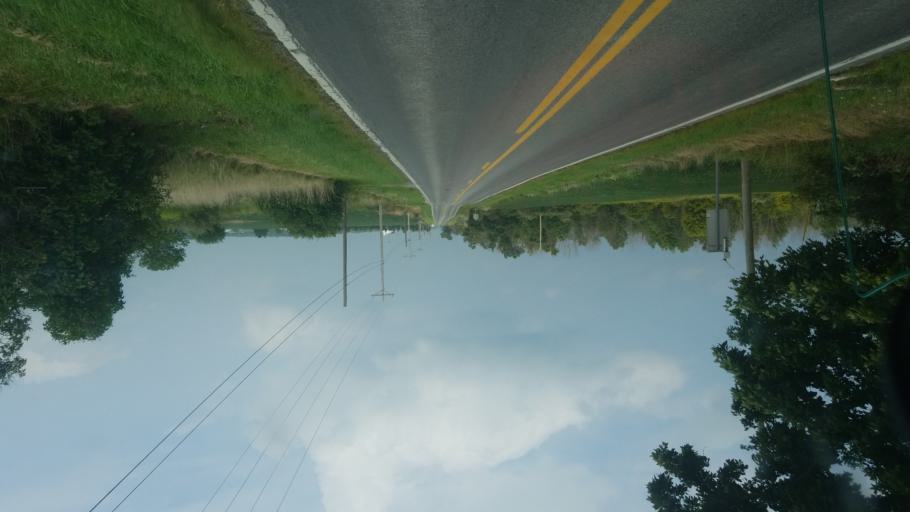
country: US
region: Ohio
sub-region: Wayne County
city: West Salem
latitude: 41.0567
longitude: -82.1703
